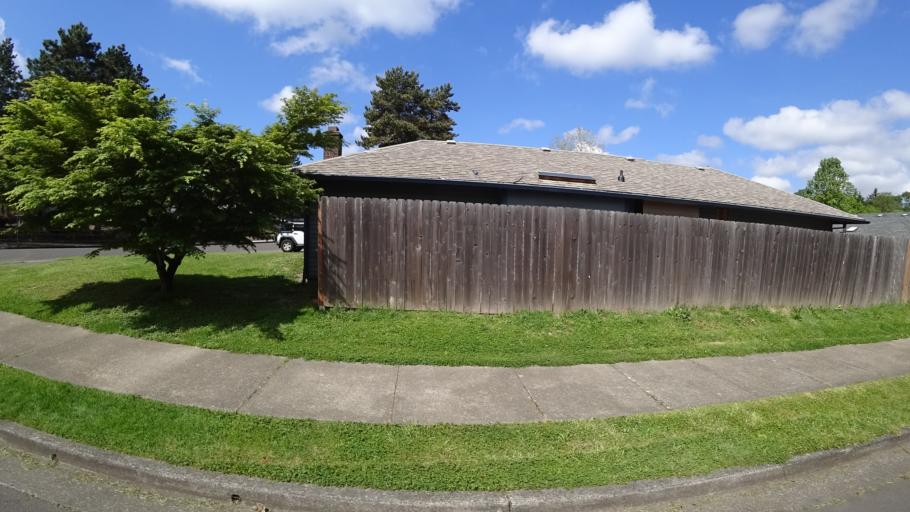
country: US
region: Oregon
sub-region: Washington County
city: Aloha
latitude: 45.5053
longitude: -122.8844
